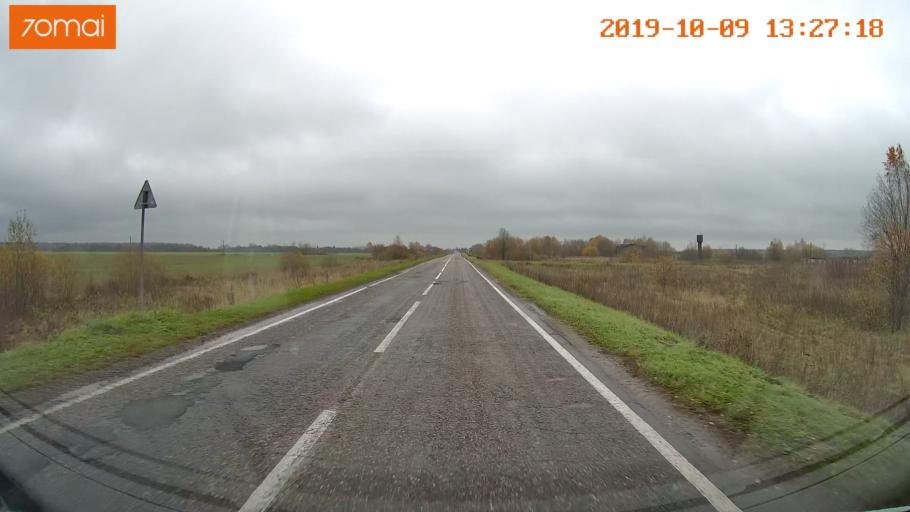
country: RU
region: Jaroslavl
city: Lyubim
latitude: 58.3161
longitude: 40.9436
